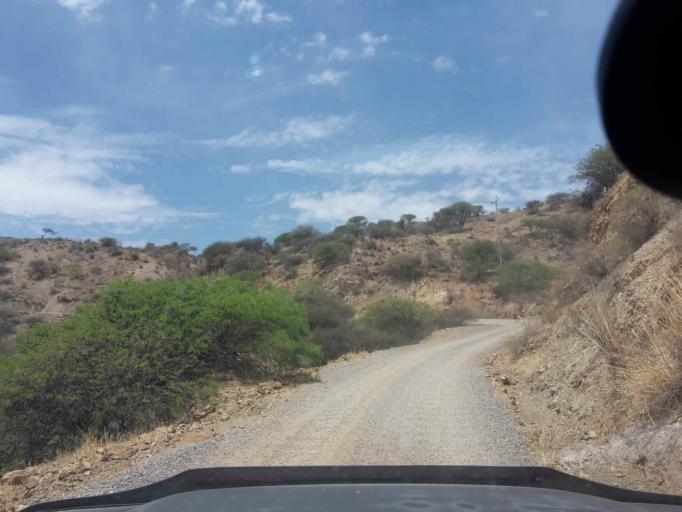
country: BO
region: Cochabamba
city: Sipe Sipe
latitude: -17.5468
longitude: -66.4802
